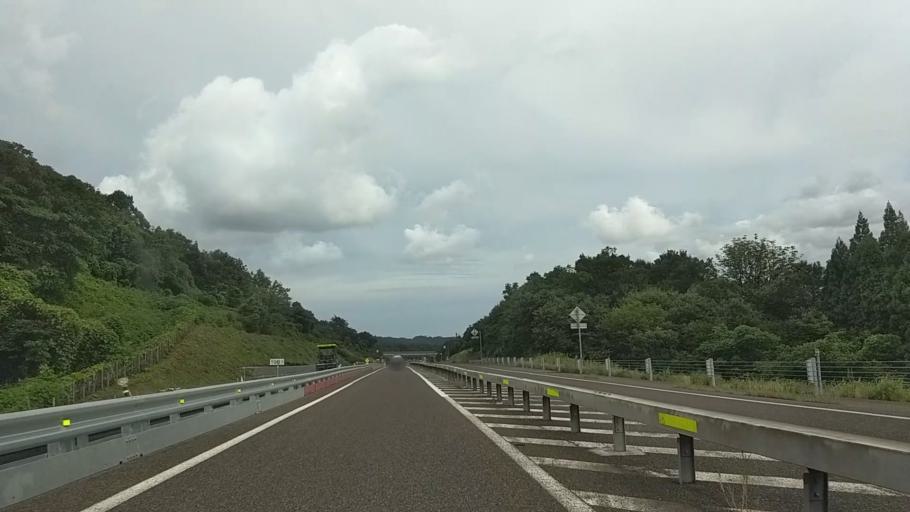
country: JP
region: Niigata
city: Arai
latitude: 37.0692
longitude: 138.2248
